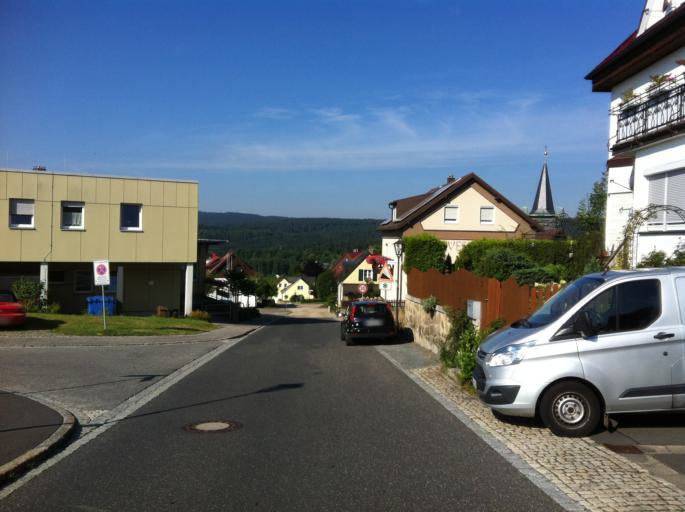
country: DE
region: Bavaria
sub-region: Upper Franconia
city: Fichtelberg
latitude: 50.0013
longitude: 11.8551
